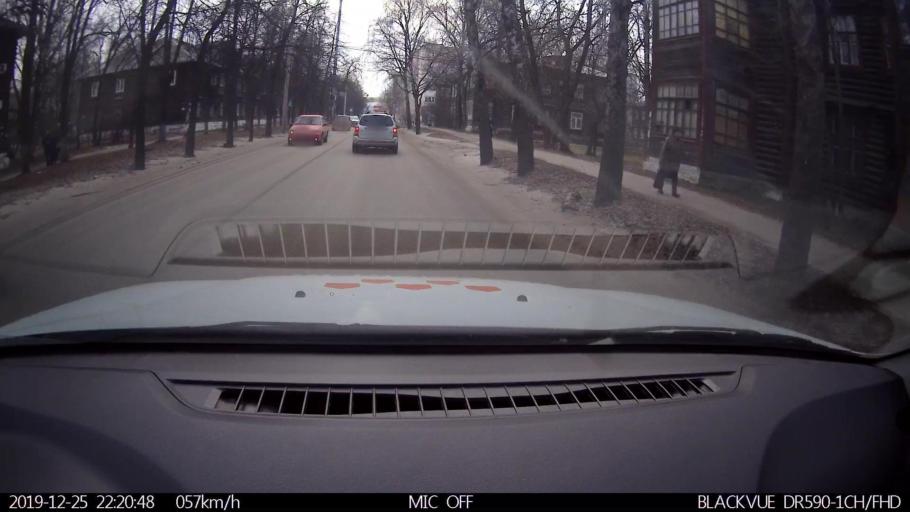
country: RU
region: Nizjnij Novgorod
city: Gorbatovka
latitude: 56.3341
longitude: 43.8398
